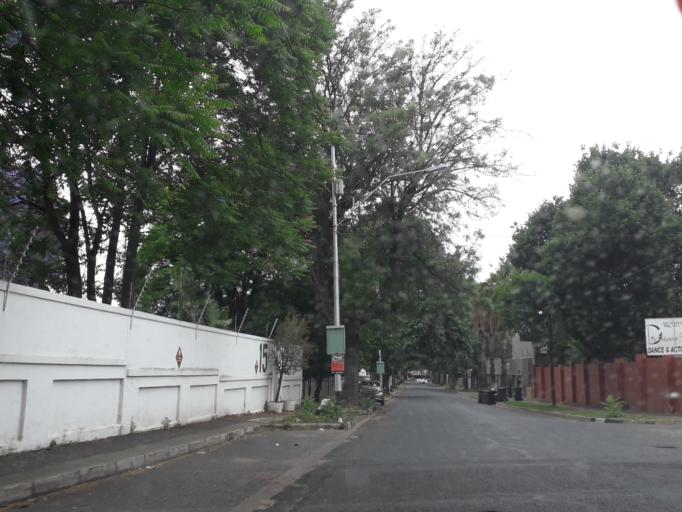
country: ZA
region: Gauteng
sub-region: City of Johannesburg Metropolitan Municipality
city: Johannesburg
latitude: -26.1626
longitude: 28.0736
